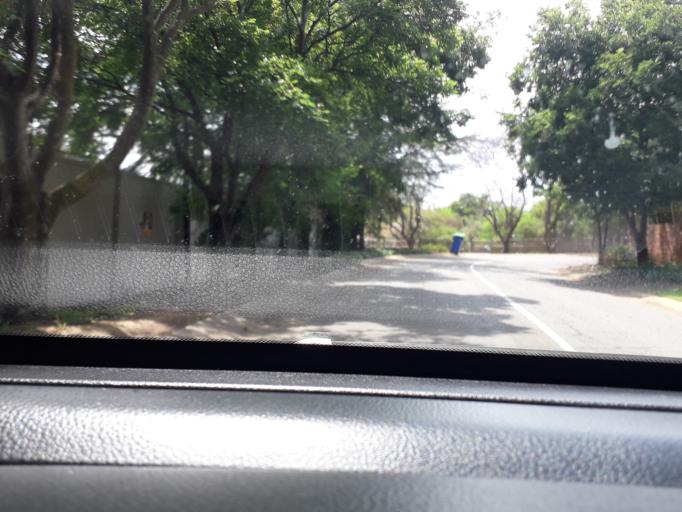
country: ZA
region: Gauteng
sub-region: City of Johannesburg Metropolitan Municipality
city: Midrand
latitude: -26.0662
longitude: 28.0463
